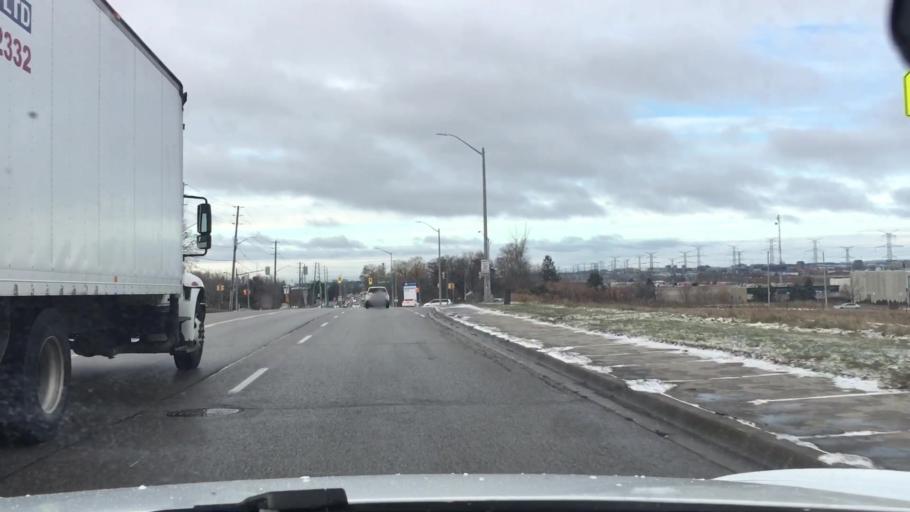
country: CA
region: Ontario
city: Markham
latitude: 43.8426
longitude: -79.3093
